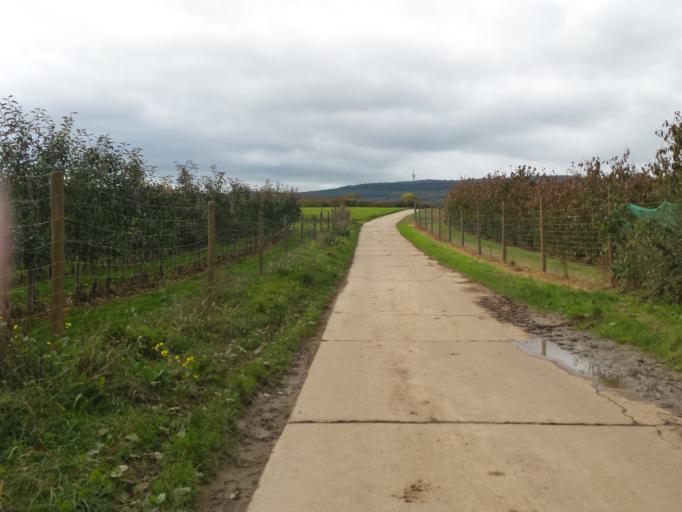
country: DE
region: Hesse
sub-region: Regierungsbezirk Darmstadt
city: Friedberg
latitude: 50.3264
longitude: 8.7231
